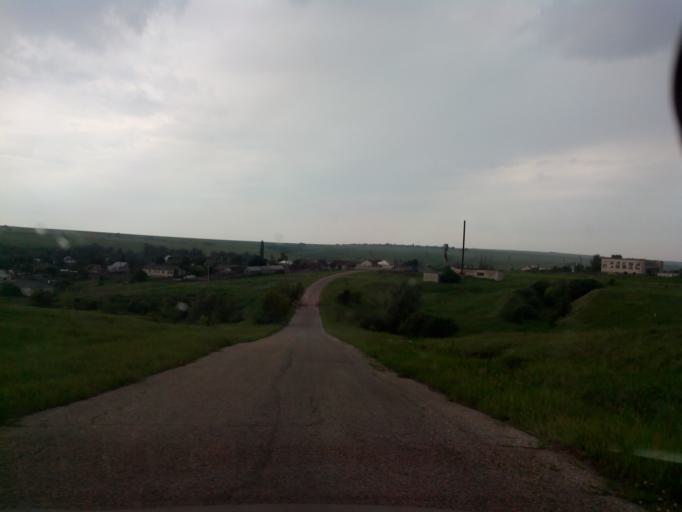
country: RU
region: Volgograd
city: Slashchevskaya
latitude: 49.7801
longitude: 42.4457
